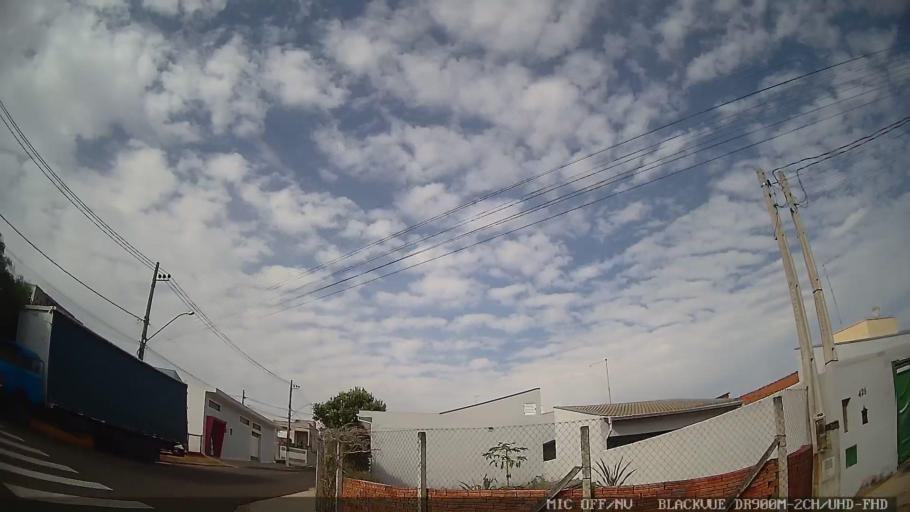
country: BR
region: Sao Paulo
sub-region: Salto
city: Salto
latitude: -23.1816
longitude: -47.2626
